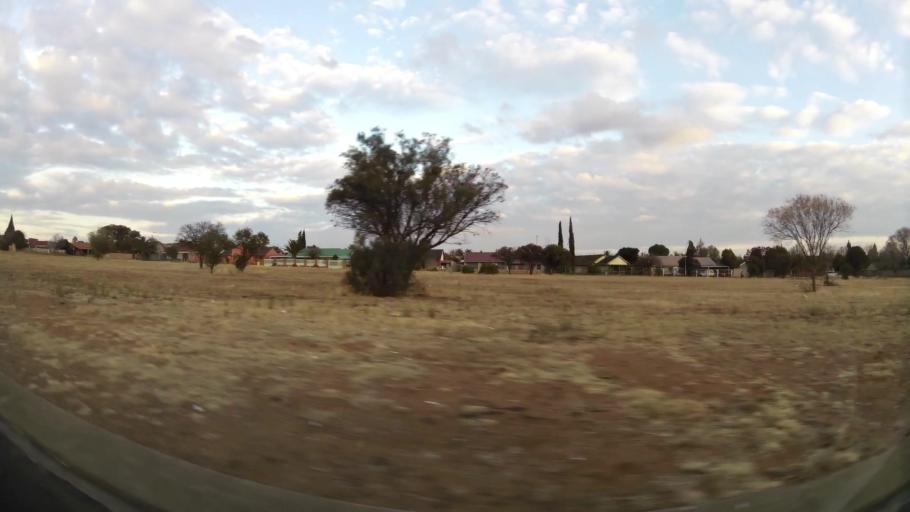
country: ZA
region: Orange Free State
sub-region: Mangaung Metropolitan Municipality
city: Bloemfontein
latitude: -29.1610
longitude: 26.1876
